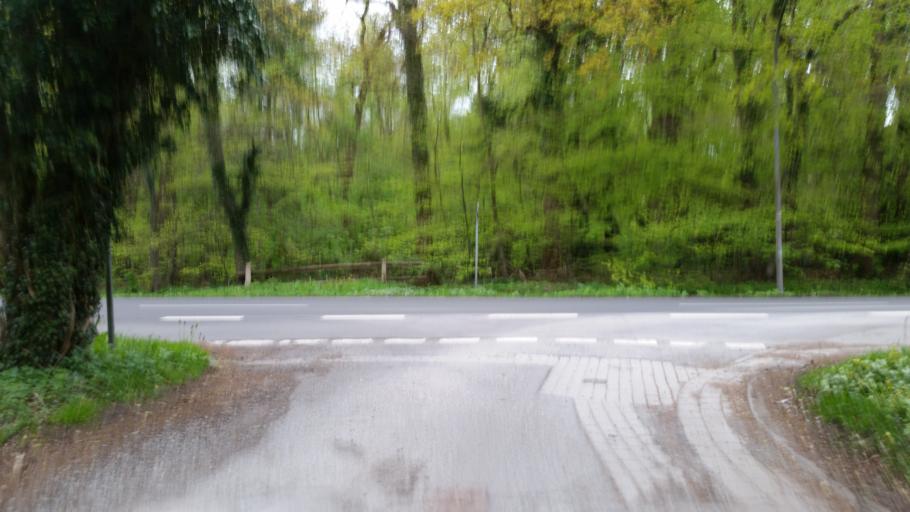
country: DE
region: Lower Saxony
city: Aurich
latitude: 53.4759
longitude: 7.4619
